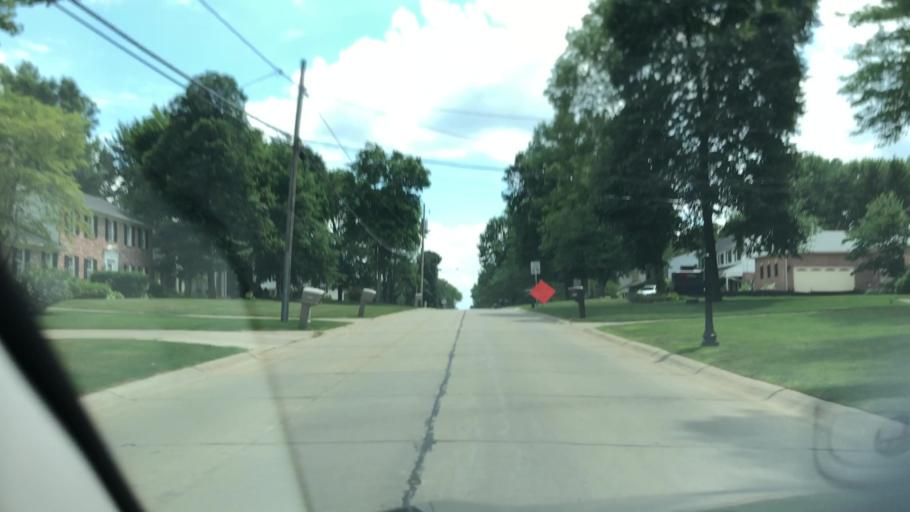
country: US
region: Ohio
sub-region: Summit County
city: Fairlawn
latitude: 41.1335
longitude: -81.6252
